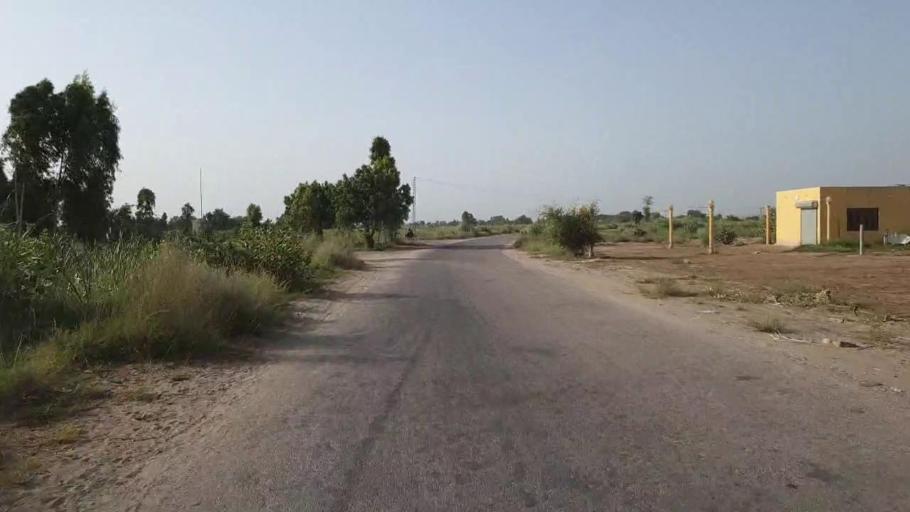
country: PK
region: Sindh
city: Jam Sahib
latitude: 26.4195
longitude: 68.8703
